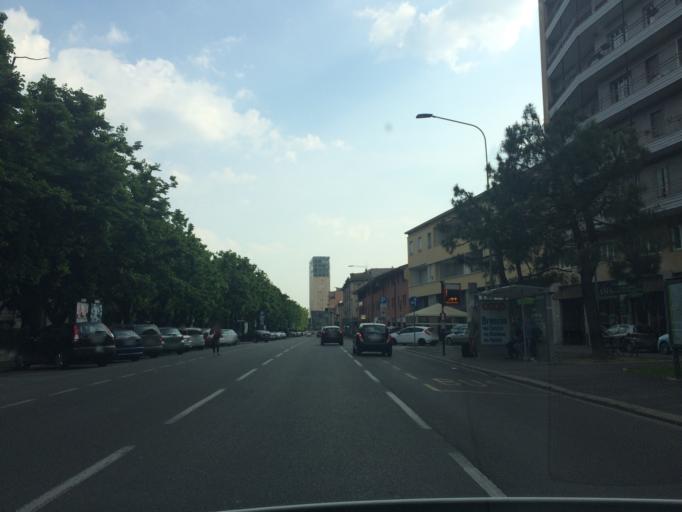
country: IT
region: Lombardy
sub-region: Provincia di Brescia
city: Brescia
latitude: 45.5411
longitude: 10.2106
